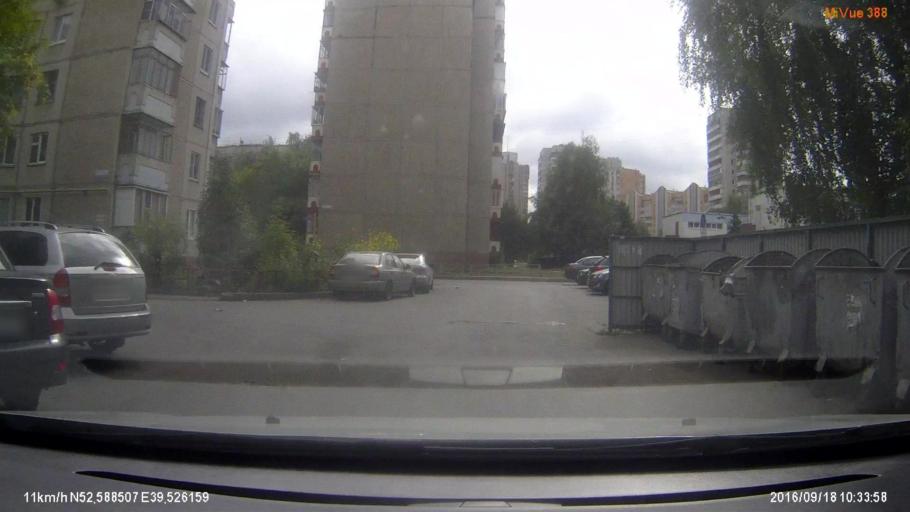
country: RU
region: Lipetsk
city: Syrskoye
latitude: 52.5897
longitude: 39.5275
